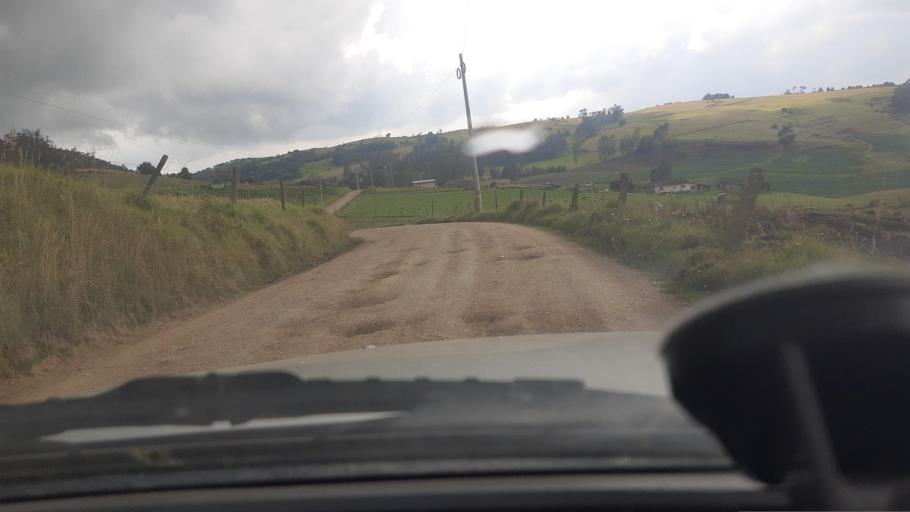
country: CO
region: Cundinamarca
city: Suesca
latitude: 5.1644
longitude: -73.7729
